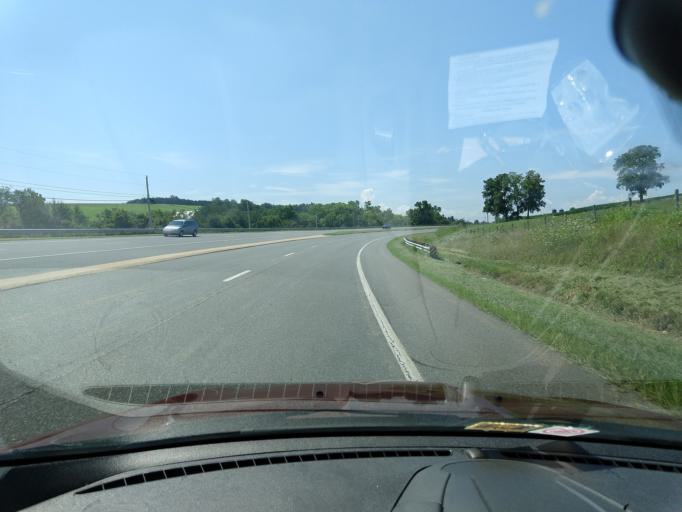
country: US
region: Virginia
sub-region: City of Harrisonburg
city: Harrisonburg
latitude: 38.5195
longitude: -78.8629
